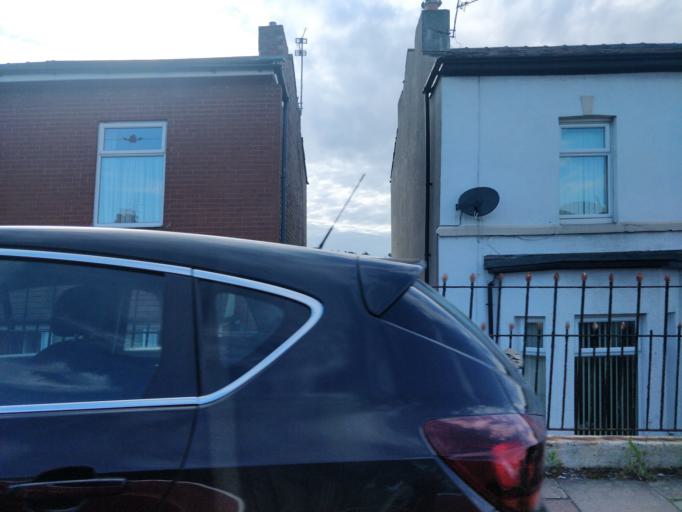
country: GB
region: England
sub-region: Sefton
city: Southport
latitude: 53.6445
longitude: -2.9883
